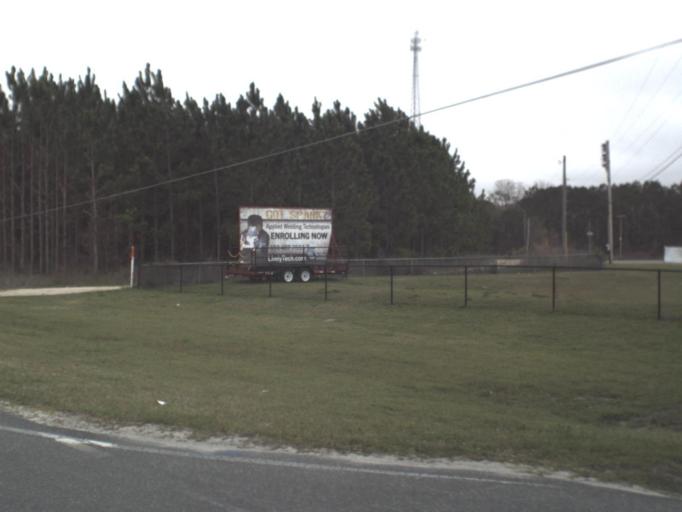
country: US
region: Florida
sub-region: Wakulla County
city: Crawfordville
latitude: 30.1086
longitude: -84.3778
